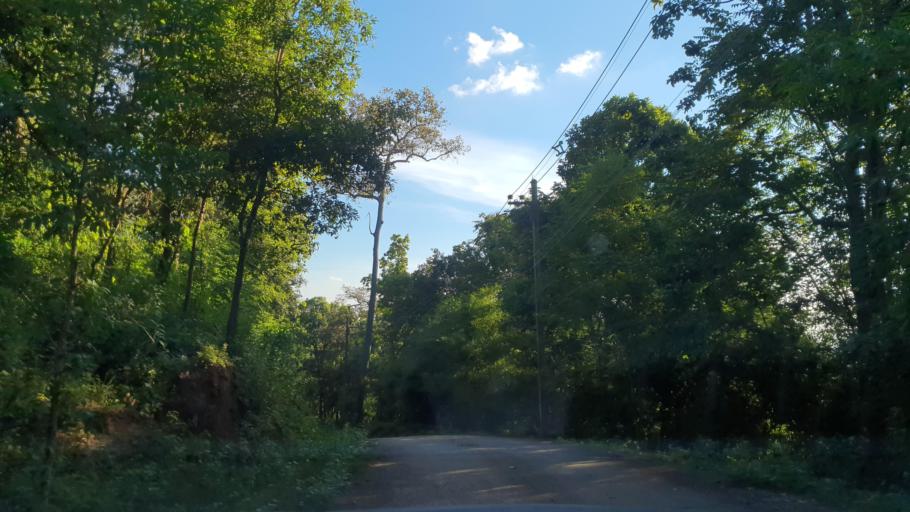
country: TH
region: Chiang Mai
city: Mae On
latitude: 18.8124
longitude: 99.3137
